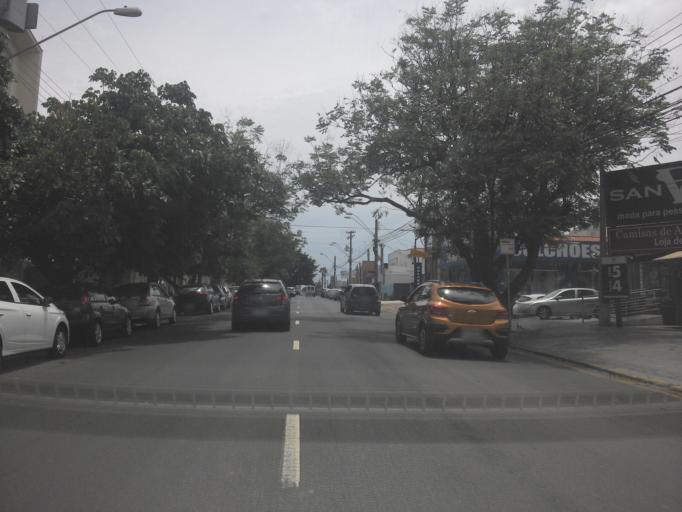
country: BR
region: Sao Paulo
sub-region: Campinas
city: Campinas
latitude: -22.8840
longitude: -47.0575
